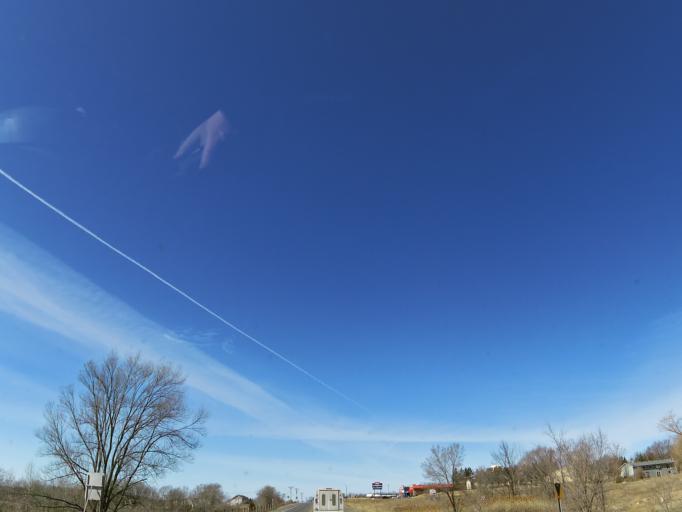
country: US
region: Minnesota
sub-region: Wright County
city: Rockford
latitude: 45.0934
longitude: -93.7493
